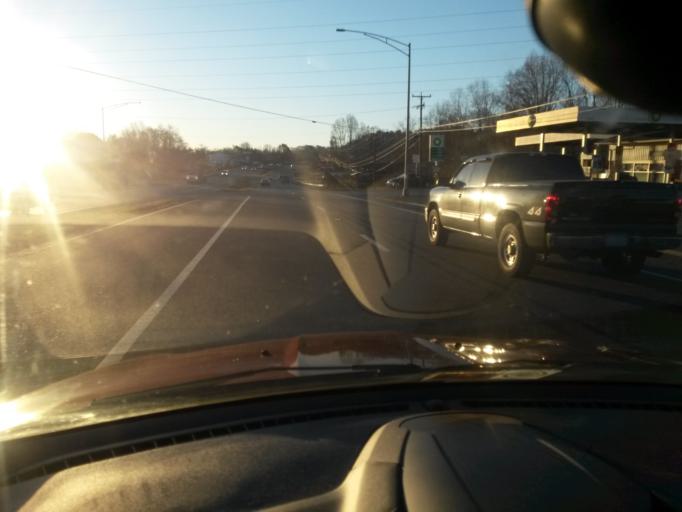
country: US
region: Virginia
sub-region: Franklin County
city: Rocky Mount
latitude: 37.0455
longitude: -79.8781
